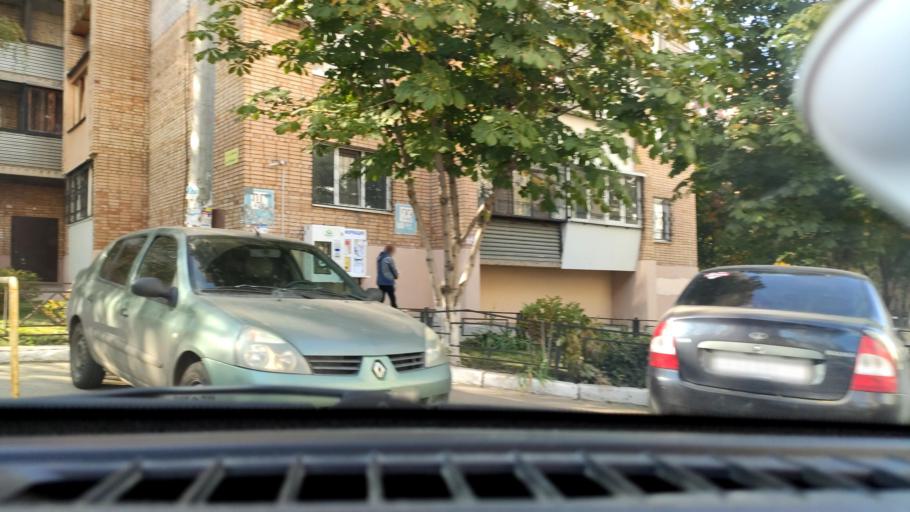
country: RU
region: Samara
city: Samara
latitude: 53.2441
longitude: 50.1865
